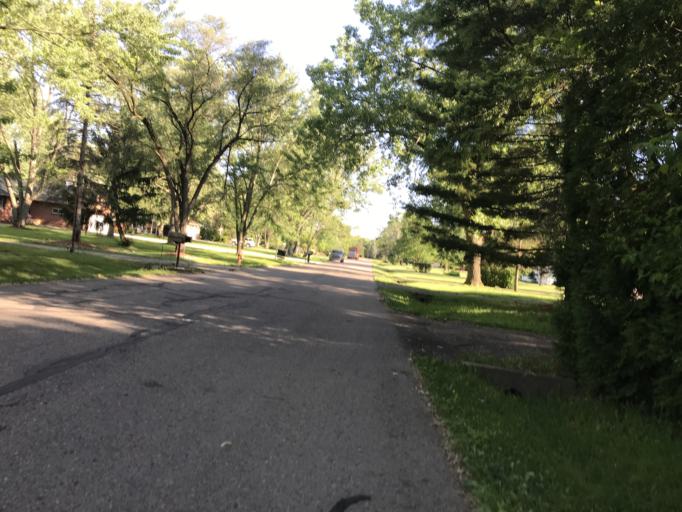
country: US
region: Michigan
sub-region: Oakland County
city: Farmington
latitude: 42.4751
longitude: -83.3489
